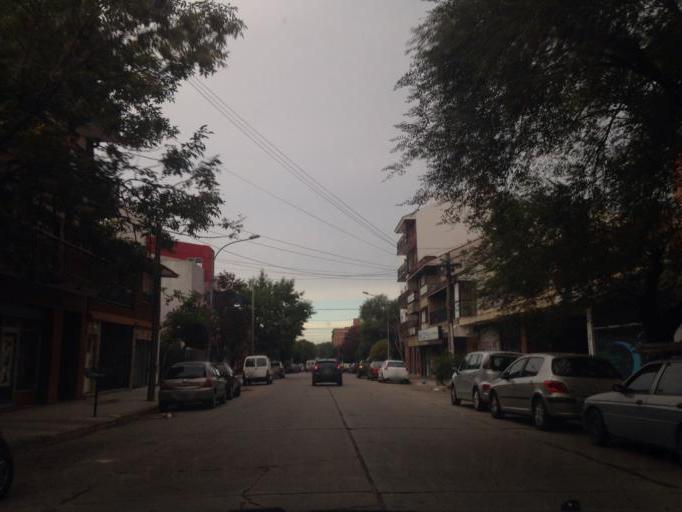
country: AR
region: Buenos Aires
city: Mar del Plata
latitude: -38.0174
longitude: -57.5695
